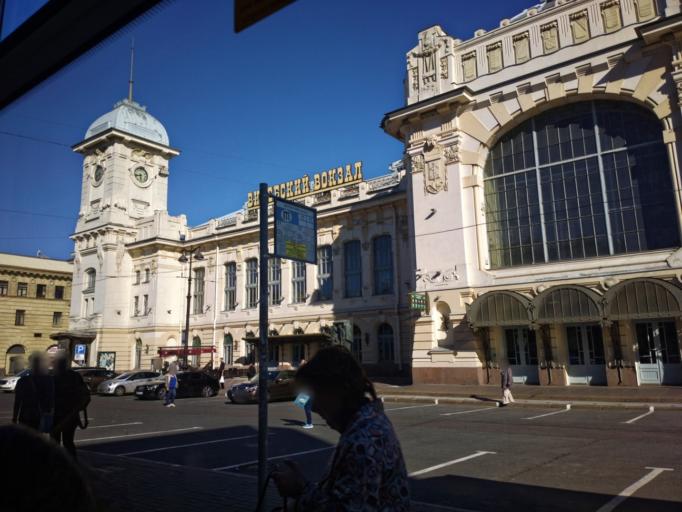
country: RU
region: St.-Petersburg
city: Saint Petersburg
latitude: 59.9202
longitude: 30.3277
